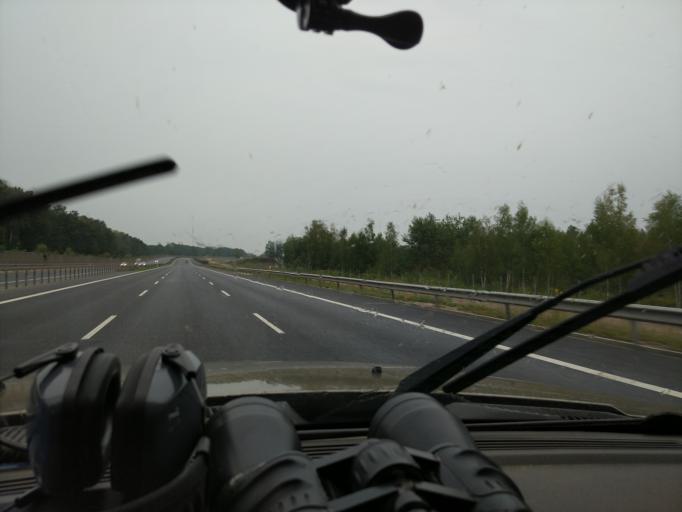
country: PL
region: Masovian Voivodeship
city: Zielonka
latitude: 52.3386
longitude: 21.1567
